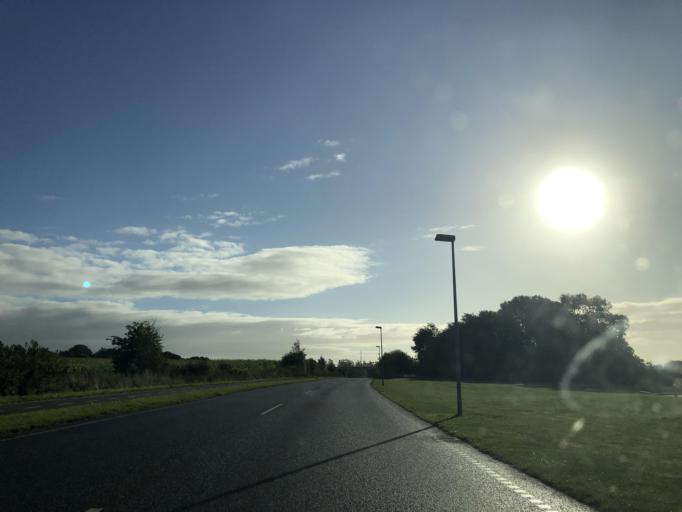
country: DK
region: Central Jutland
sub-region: Viborg Kommune
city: Viborg
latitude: 56.4580
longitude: 9.3498
